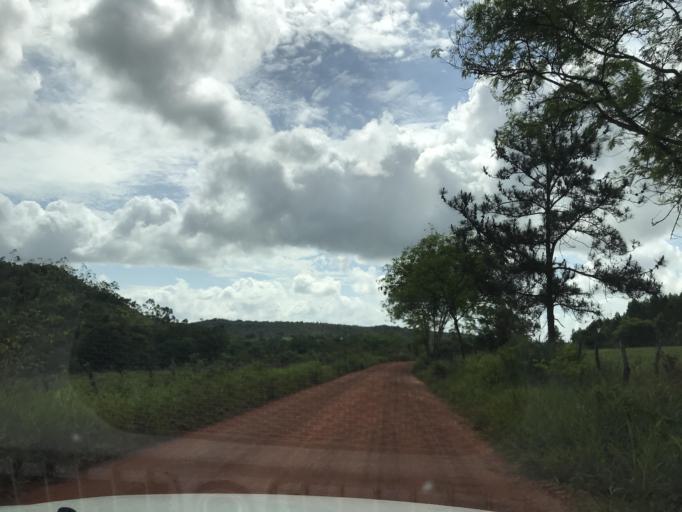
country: BR
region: Bahia
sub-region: Entre Rios
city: Entre Rios
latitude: -12.1766
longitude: -38.1280
